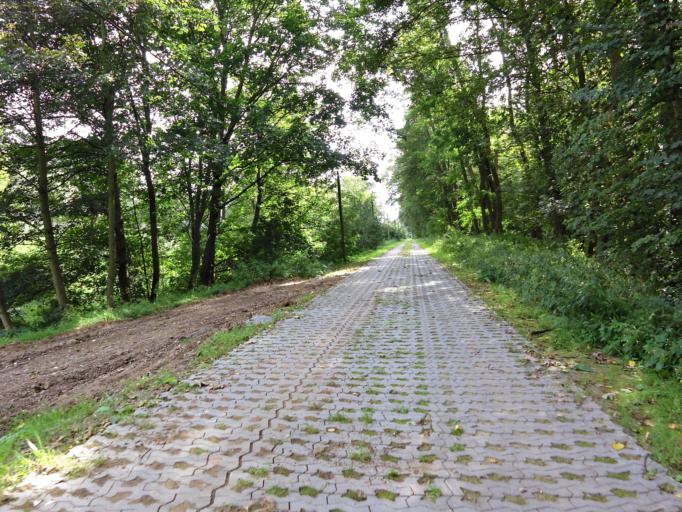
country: DE
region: Saxony-Anhalt
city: Havelberg
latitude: 52.8358
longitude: 12.0521
